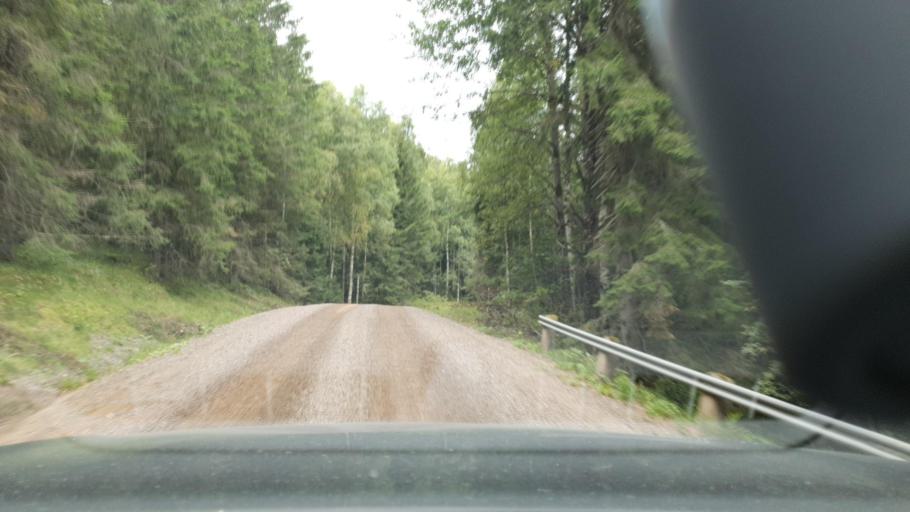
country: SE
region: Vaermland
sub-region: Eda Kommun
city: Charlottenberg
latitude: 60.0630
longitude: 12.5458
